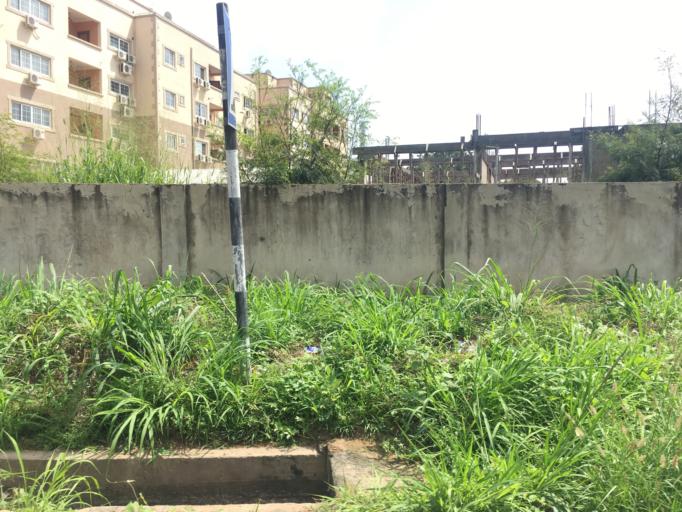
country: GH
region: Greater Accra
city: Medina Estates
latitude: 5.6346
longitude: -0.1642
